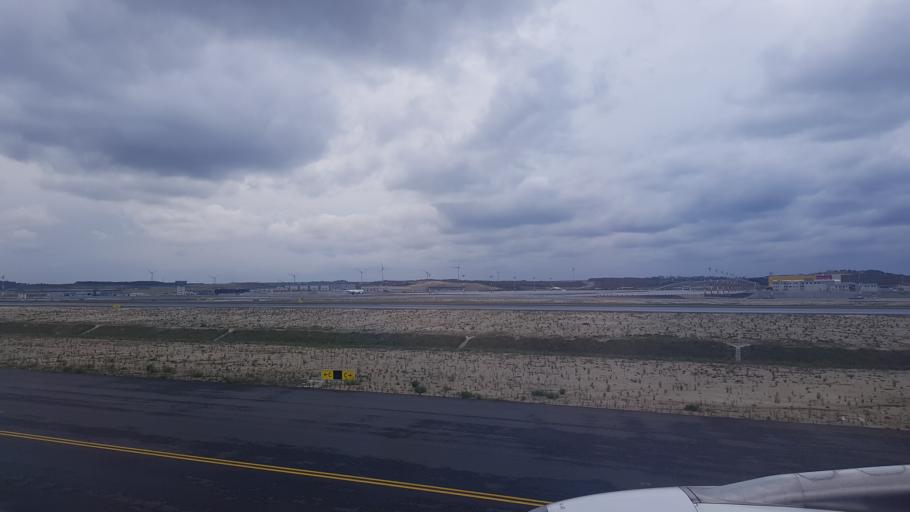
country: TR
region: Istanbul
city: Durusu
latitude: 41.2697
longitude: 28.7303
